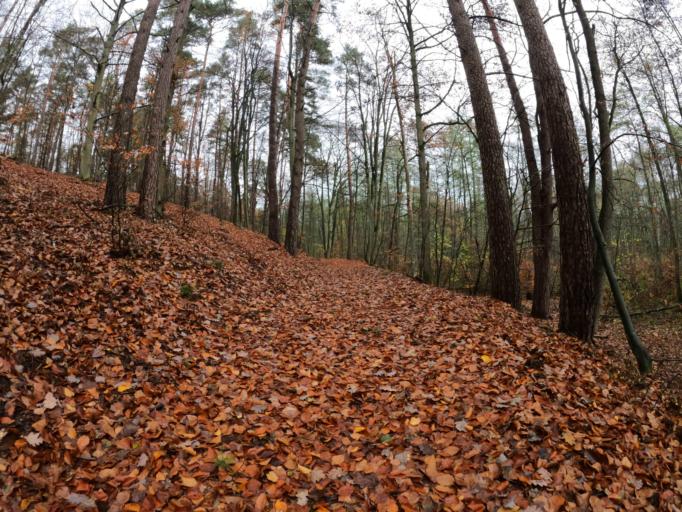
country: PL
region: West Pomeranian Voivodeship
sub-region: Powiat walecki
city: Tuczno
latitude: 53.2693
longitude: 16.2527
